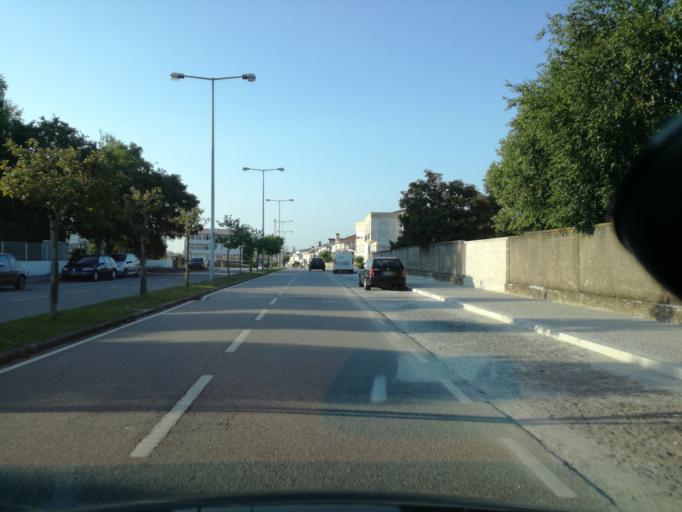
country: PT
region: Porto
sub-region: Maia
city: Milheiros
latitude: 41.2147
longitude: -8.6000
